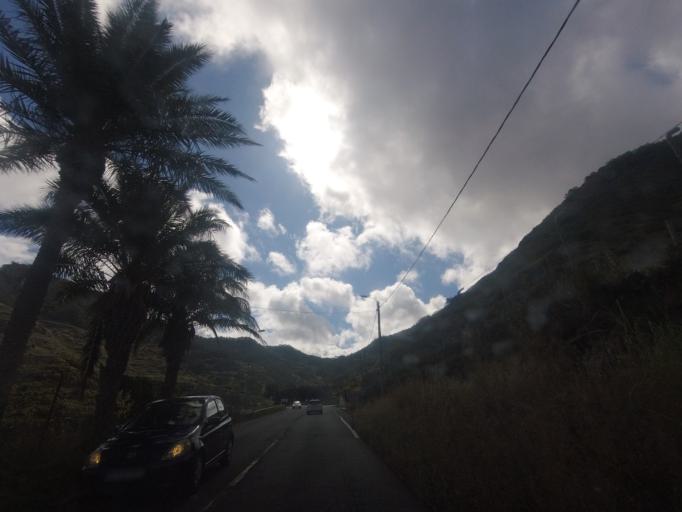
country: PT
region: Madeira
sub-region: Machico
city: Canical
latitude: 32.7385
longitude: -16.7497
